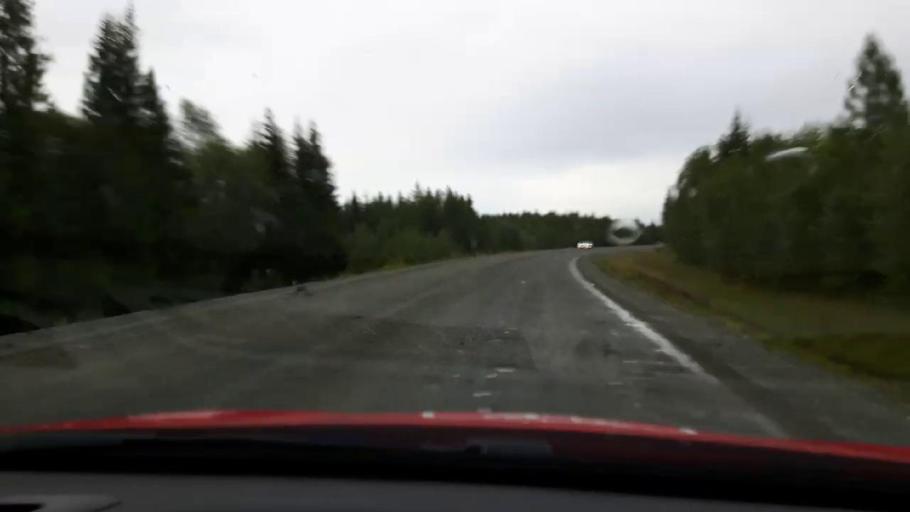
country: SE
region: Jaemtland
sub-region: Are Kommun
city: Are
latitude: 63.4109
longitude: 12.7912
